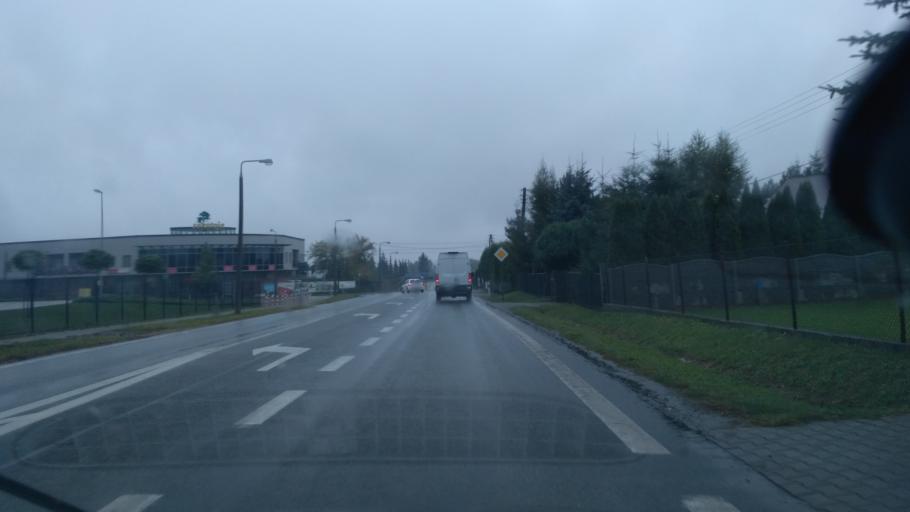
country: PL
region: Subcarpathian Voivodeship
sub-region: Powiat debicki
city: Debica
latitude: 50.0604
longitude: 21.4461
